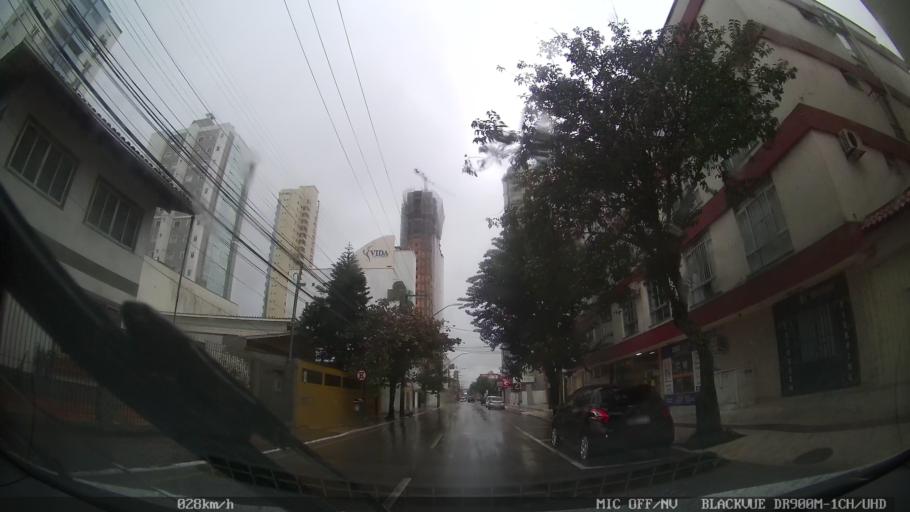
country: BR
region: Santa Catarina
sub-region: Balneario Camboriu
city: Balneario Camboriu
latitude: -26.9886
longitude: -48.6380
